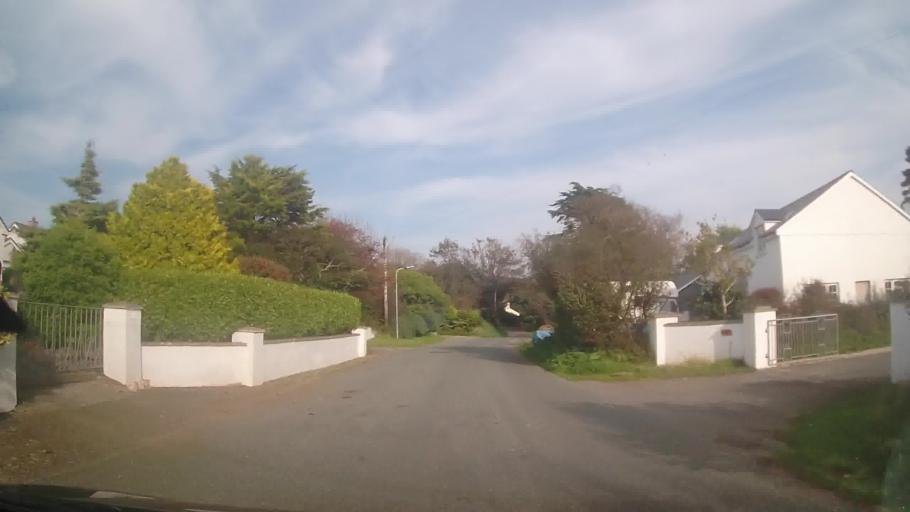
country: GB
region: Wales
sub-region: Pembrokeshire
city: Camrose
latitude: 51.8483
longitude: -5.0817
